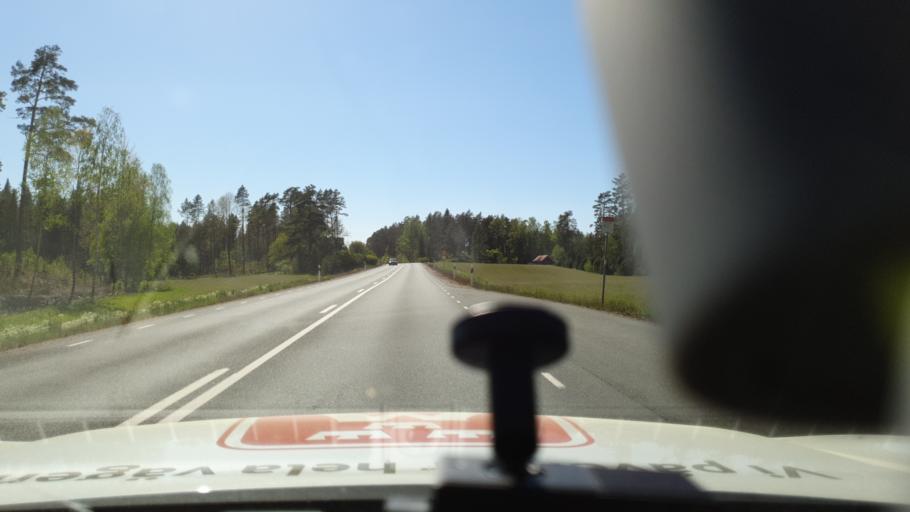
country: SE
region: Kalmar
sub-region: Hultsfreds Kommun
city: Virserum
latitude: 57.3987
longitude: 15.4002
